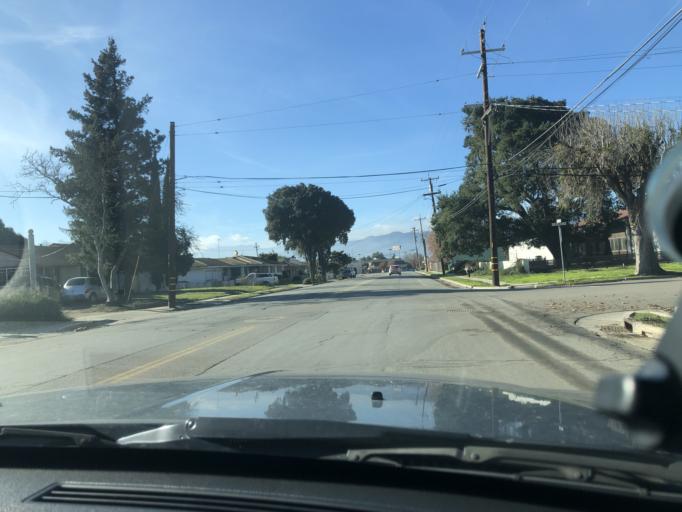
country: US
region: California
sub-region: Monterey County
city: King City
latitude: 36.2061
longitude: -121.1287
